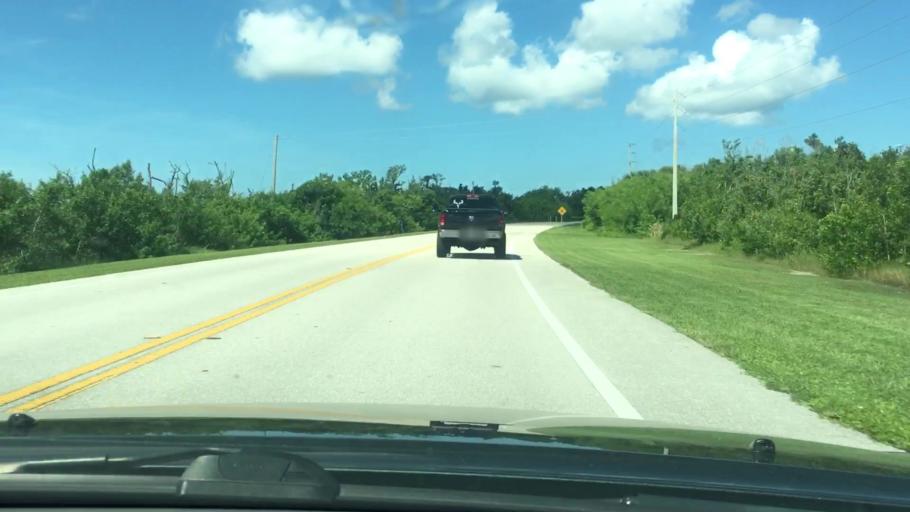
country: US
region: Florida
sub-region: Collier County
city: Marco
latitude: 25.9318
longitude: -81.6719
